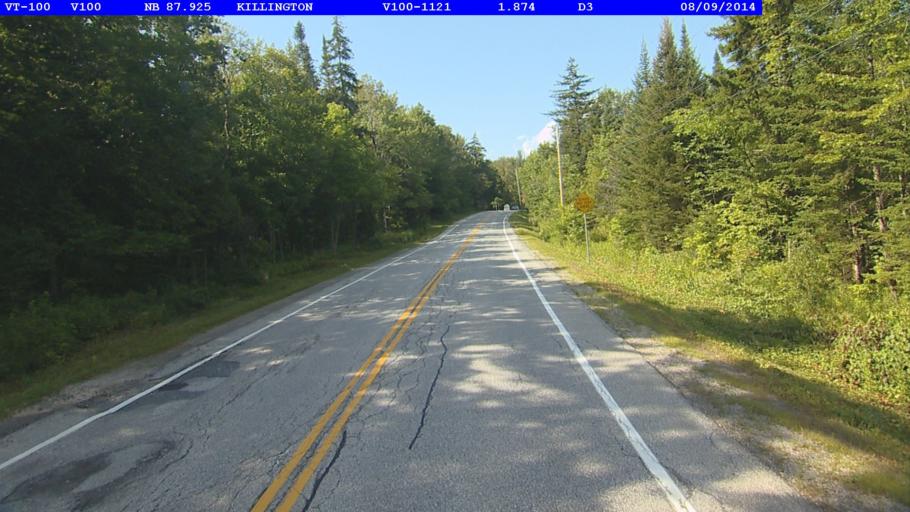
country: US
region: Vermont
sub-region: Rutland County
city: Rutland
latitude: 43.6922
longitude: -72.8137
